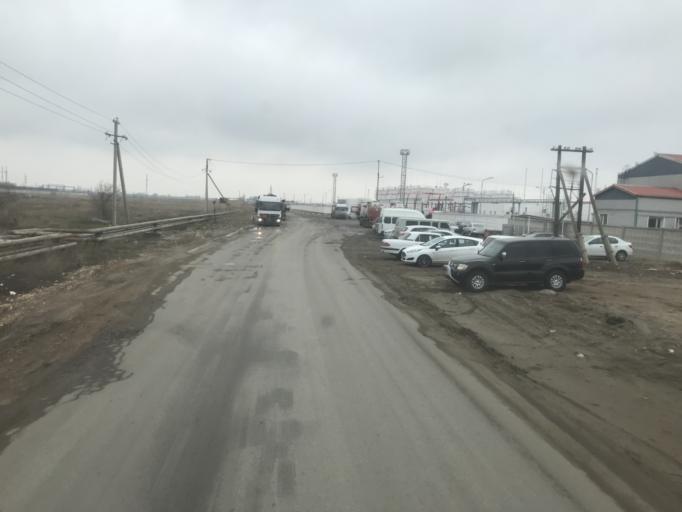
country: RU
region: Volgograd
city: Svetlyy Yar
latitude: 48.5091
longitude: 44.6404
